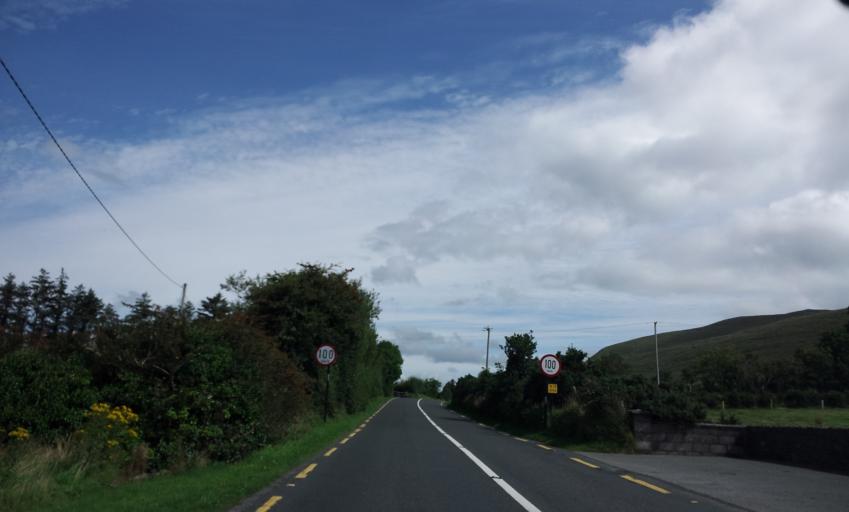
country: IE
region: Munster
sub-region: Ciarrai
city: Killorglin
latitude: 52.0592
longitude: -9.9281
